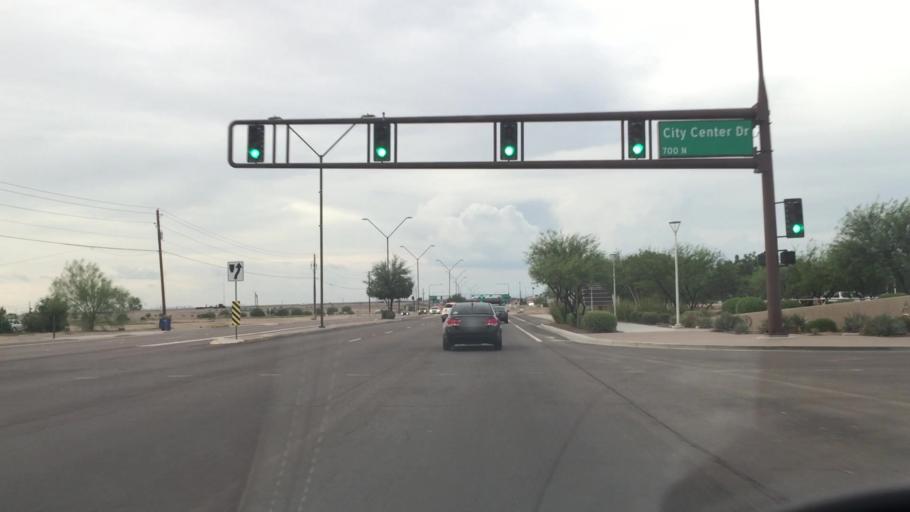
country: US
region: Arizona
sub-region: Maricopa County
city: Tolleson
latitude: 33.4540
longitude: -112.3062
